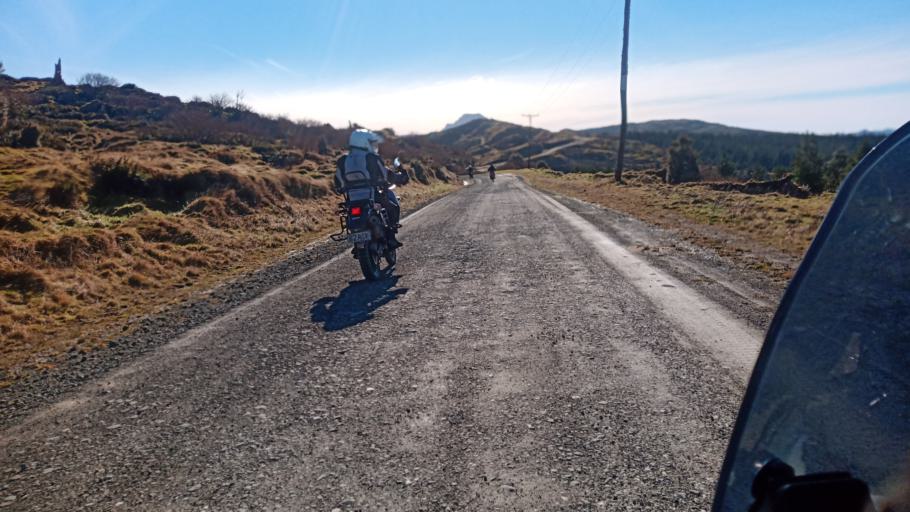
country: NZ
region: Gisborne
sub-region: Gisborne District
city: Gisborne
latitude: -38.1849
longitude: 177.8209
